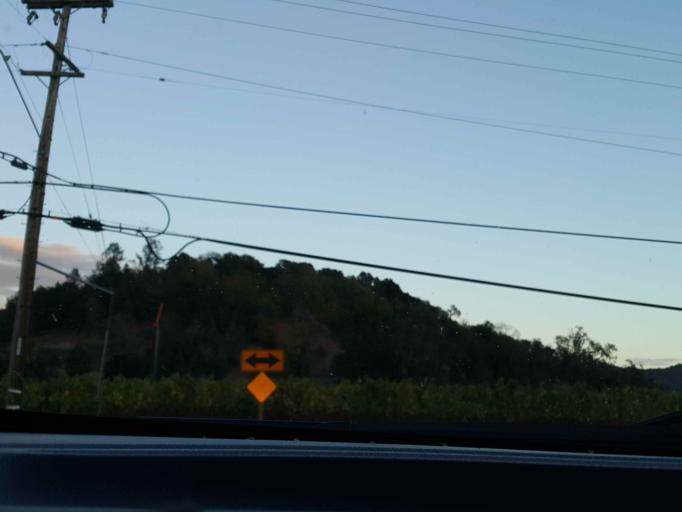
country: US
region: California
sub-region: Napa County
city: Yountville
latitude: 38.4224
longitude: -122.3473
